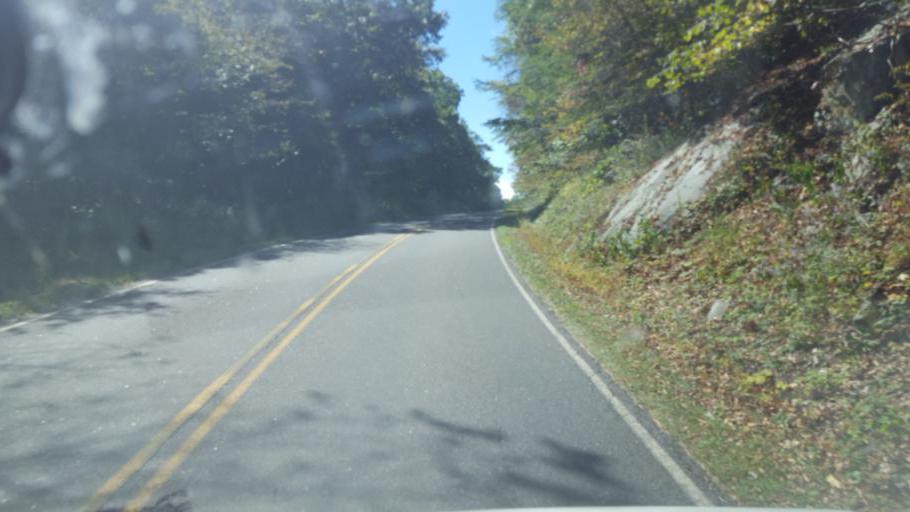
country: US
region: Virginia
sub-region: Page County
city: Stanley
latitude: 38.4585
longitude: -78.4625
